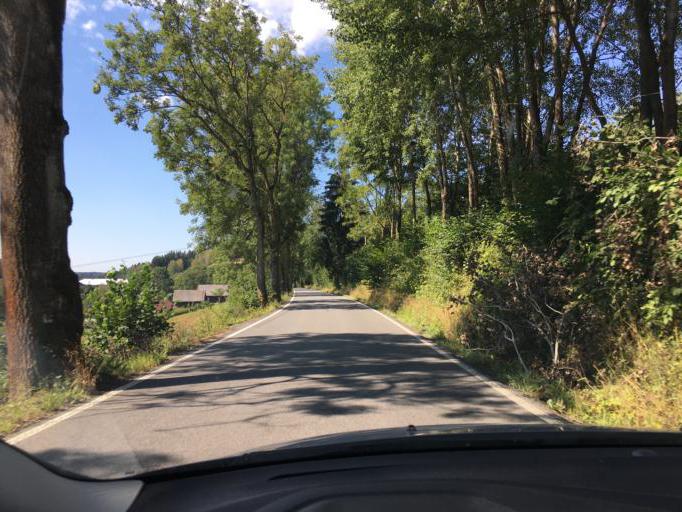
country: CZ
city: Plavy
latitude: 50.7015
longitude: 15.3607
